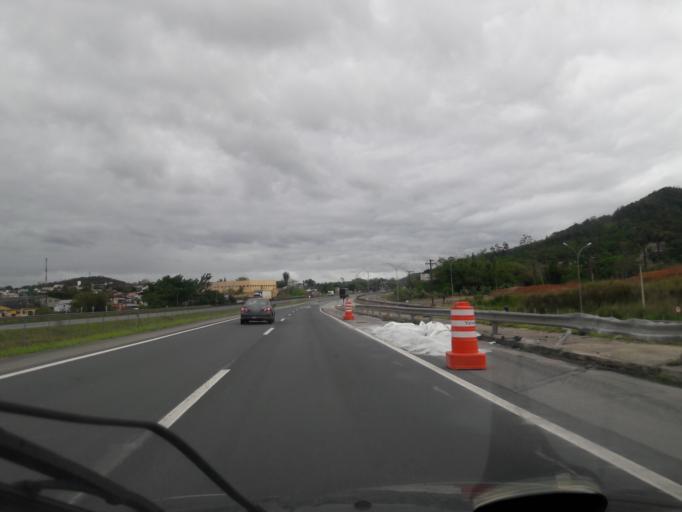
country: BR
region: Sao Paulo
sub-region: Miracatu
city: Miracatu
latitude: -24.2884
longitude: -47.4595
